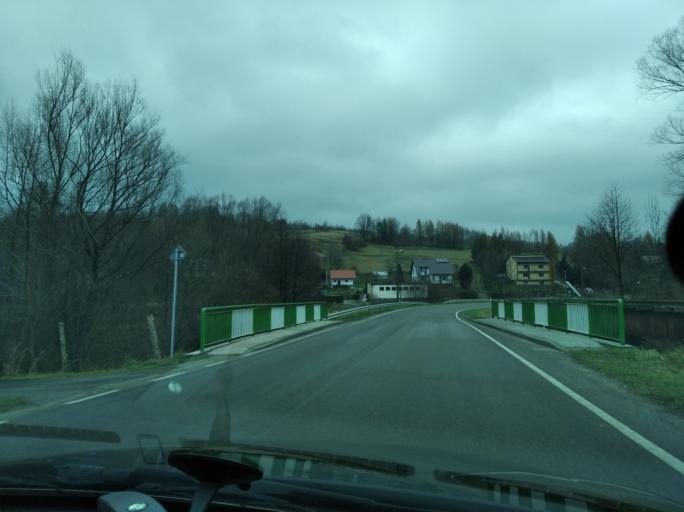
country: PL
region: Subcarpathian Voivodeship
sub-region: Powiat przeworski
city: Jawornik Polski
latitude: 49.9123
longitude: 22.2984
